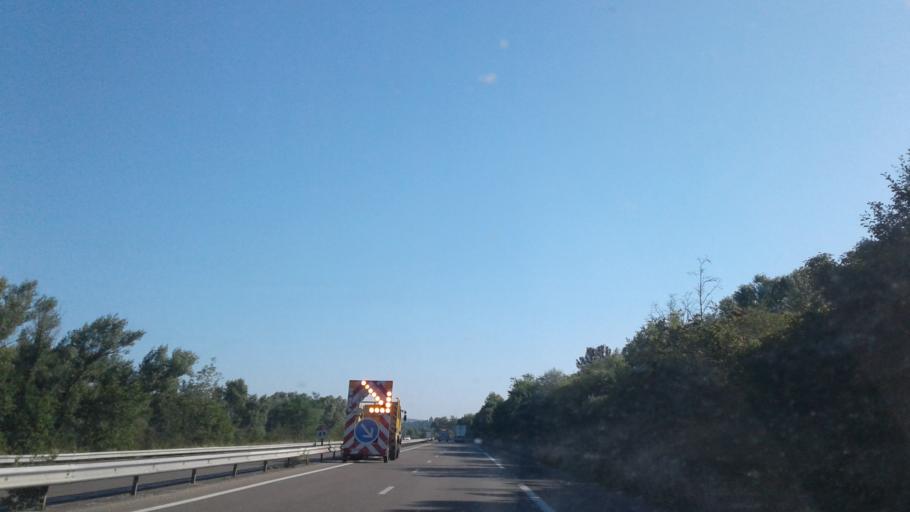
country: FR
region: Rhone-Alpes
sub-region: Departement de l'Ain
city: Priay
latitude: 46.0373
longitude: 5.3212
